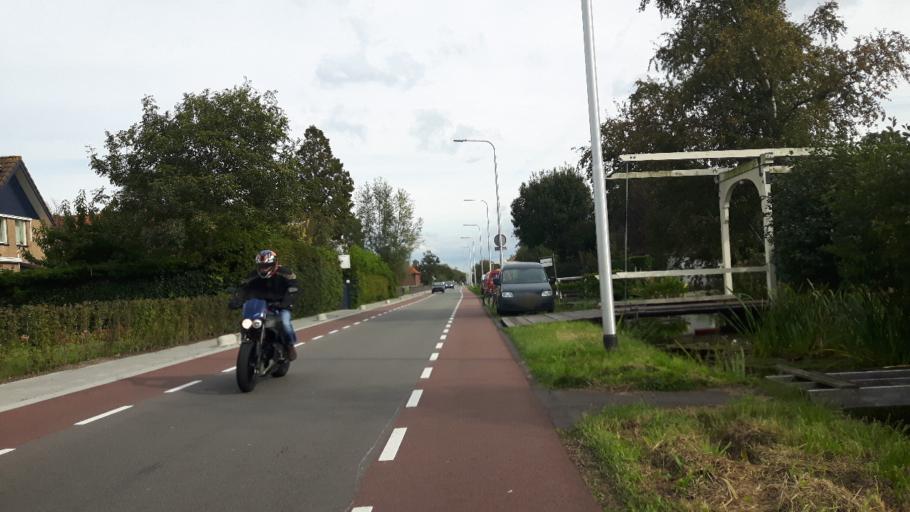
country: NL
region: Utrecht
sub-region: Gemeente De Ronde Venen
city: Mijdrecht
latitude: 52.1655
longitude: 4.8417
